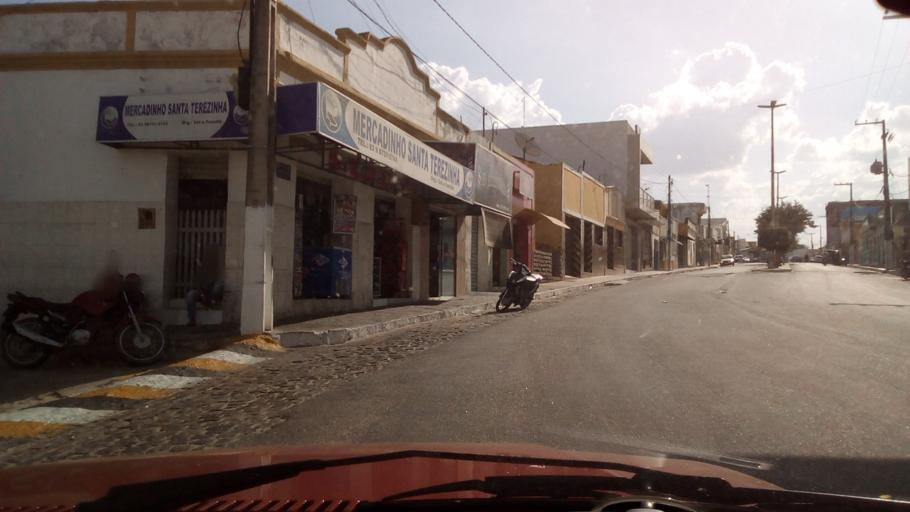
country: BR
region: Paraiba
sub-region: Arara
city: Arara
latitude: -6.8293
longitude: -35.7596
